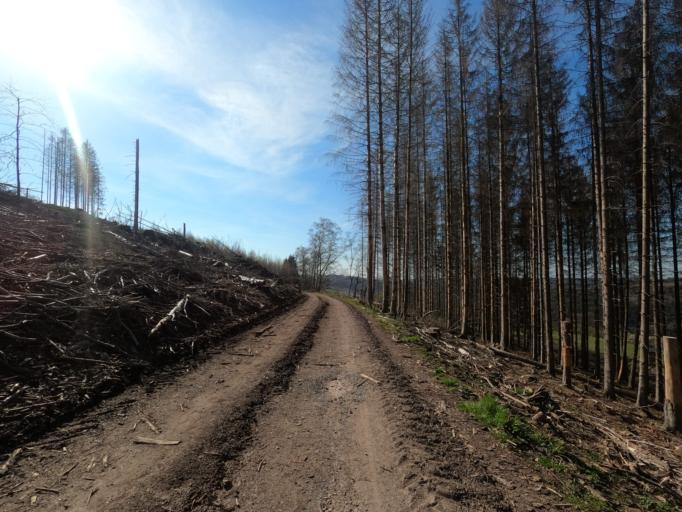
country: DE
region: North Rhine-Westphalia
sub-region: Regierungsbezirk Arnsberg
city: Herscheid
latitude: 51.1779
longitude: 7.7320
